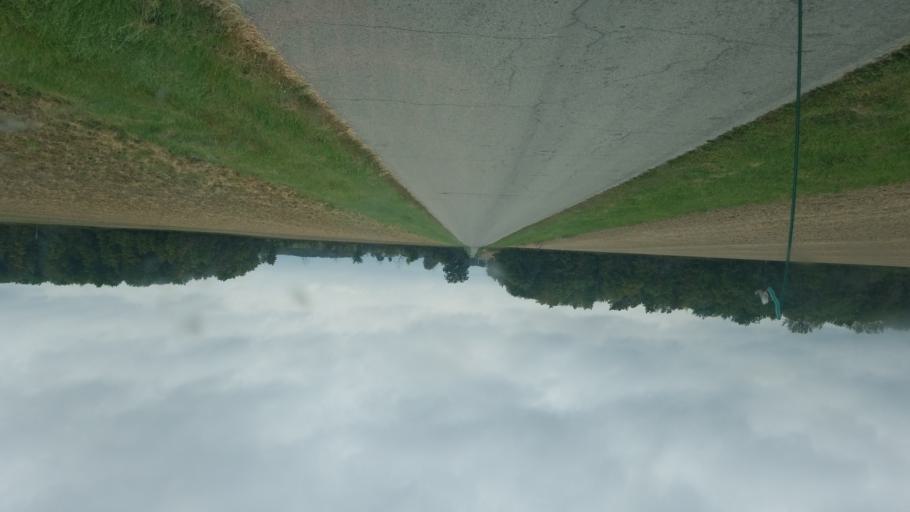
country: US
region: Ohio
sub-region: Seneca County
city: Fostoria
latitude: 41.0684
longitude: -83.4961
